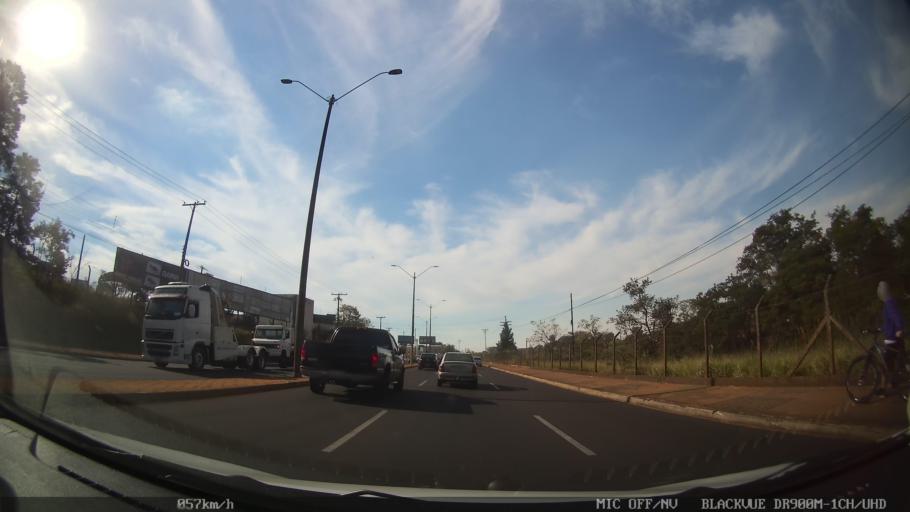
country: BR
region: Sao Paulo
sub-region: Araraquara
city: Araraquara
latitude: -21.7715
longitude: -48.1654
